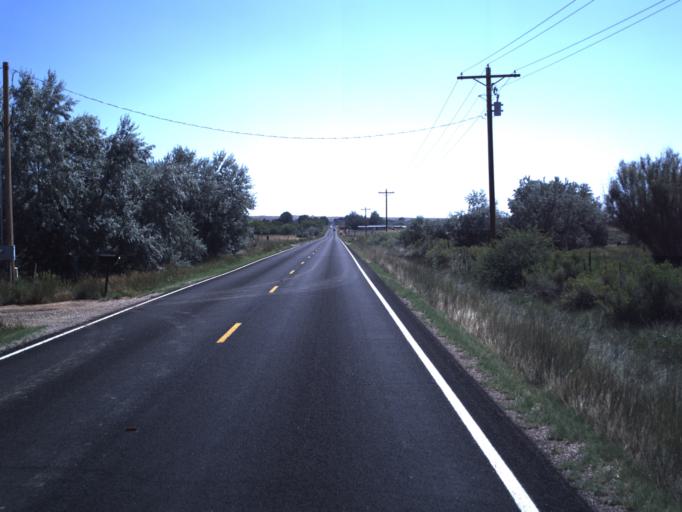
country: US
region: Utah
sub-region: Duchesne County
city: Roosevelt
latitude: 40.4037
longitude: -109.8328
